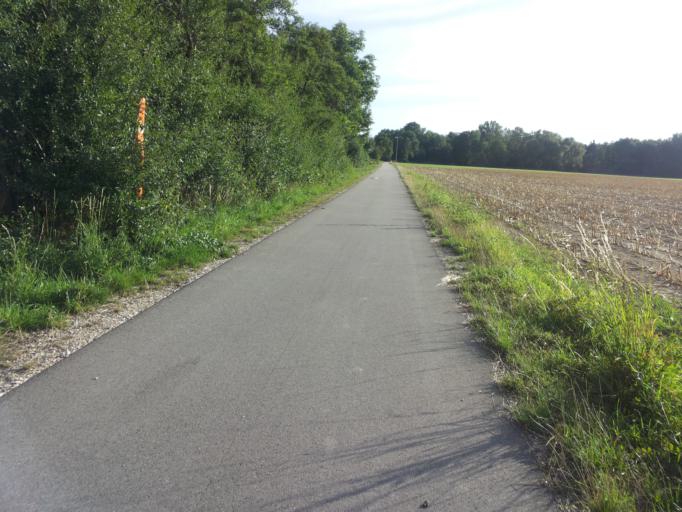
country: DE
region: Bavaria
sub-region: Upper Bavaria
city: Gaimersheim
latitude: 48.7880
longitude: 11.3711
